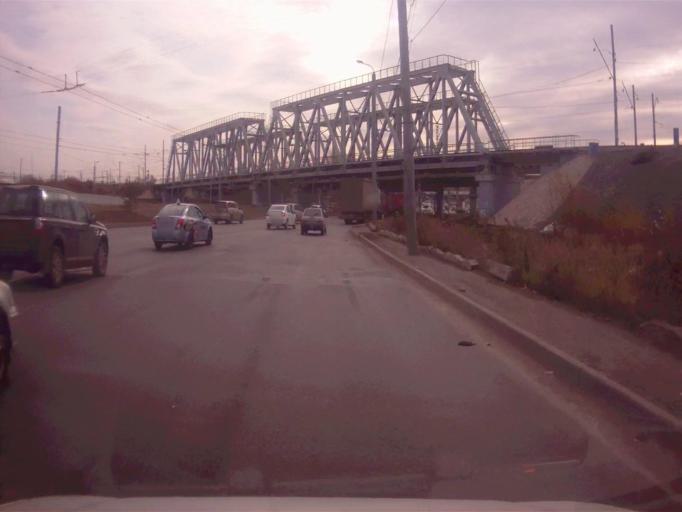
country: RU
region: Chelyabinsk
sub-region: Gorod Chelyabinsk
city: Chelyabinsk
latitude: 55.1551
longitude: 61.4430
